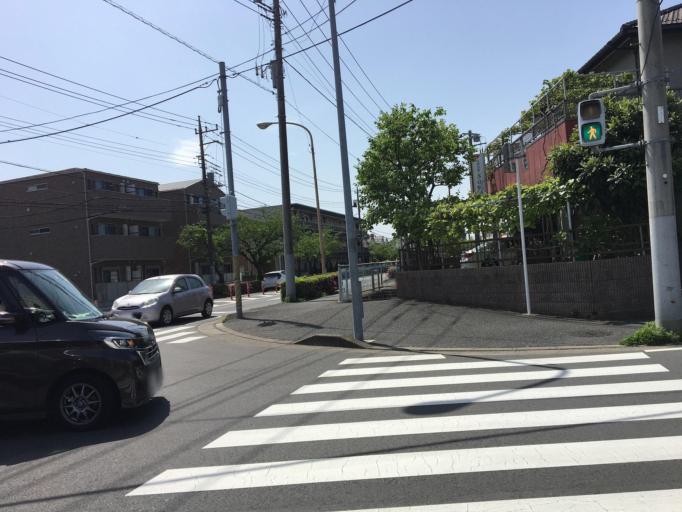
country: JP
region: Chiba
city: Nagareyama
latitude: 35.8439
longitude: 139.9015
